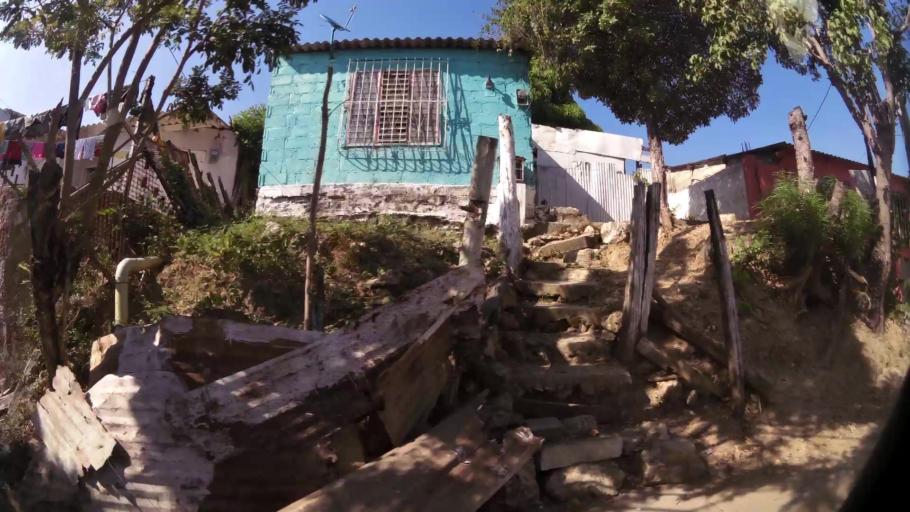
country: CO
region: Bolivar
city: Cartagena
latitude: 10.3941
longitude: -75.5016
